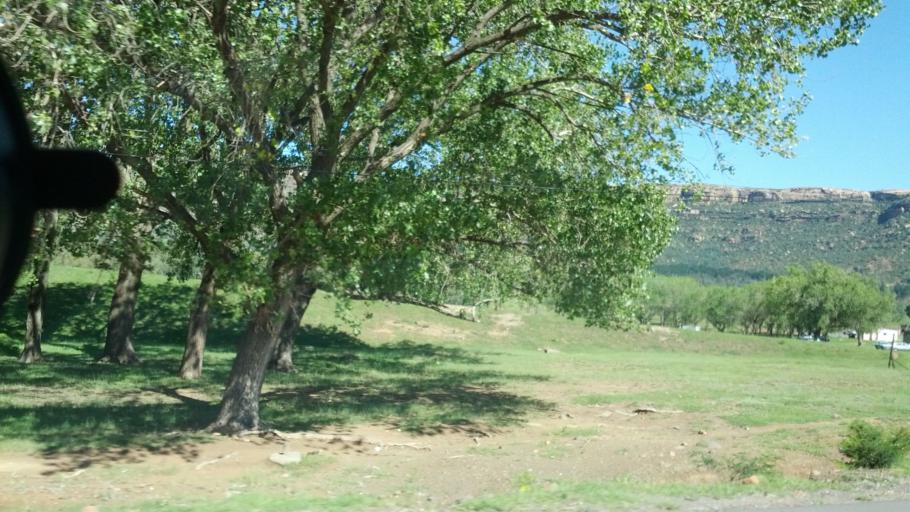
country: LS
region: Maseru
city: Nako
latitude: -29.6207
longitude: 27.4971
